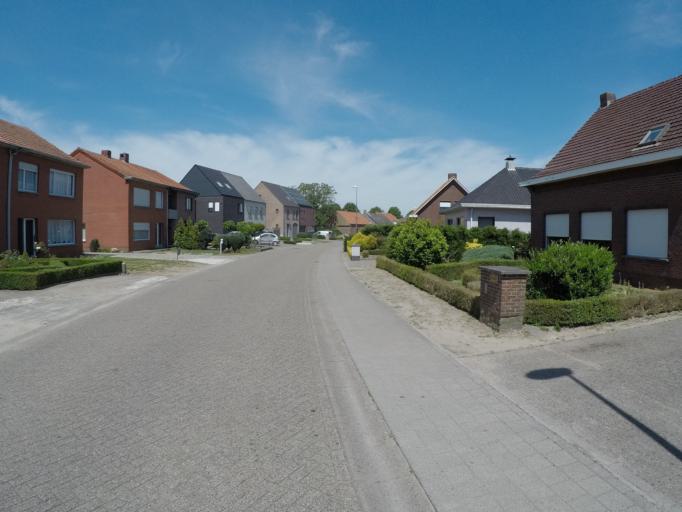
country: BE
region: Flanders
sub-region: Provincie Antwerpen
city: Wuustwezel
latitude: 51.3964
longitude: 4.5956
